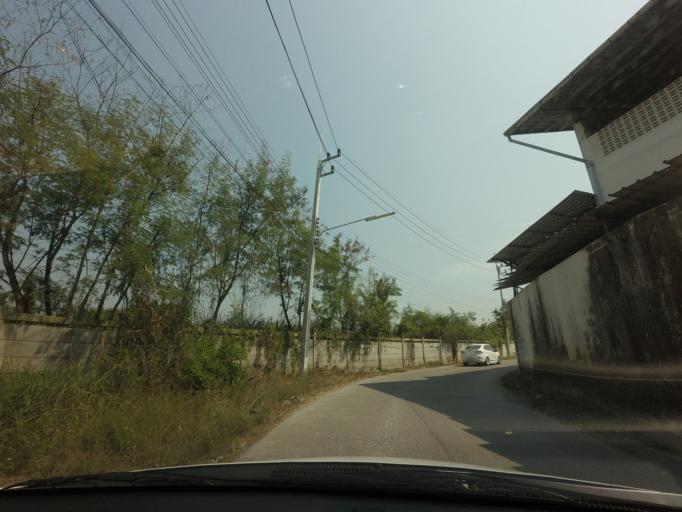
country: TH
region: Nakhon Pathom
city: Sam Phran
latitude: 13.7270
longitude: 100.2667
